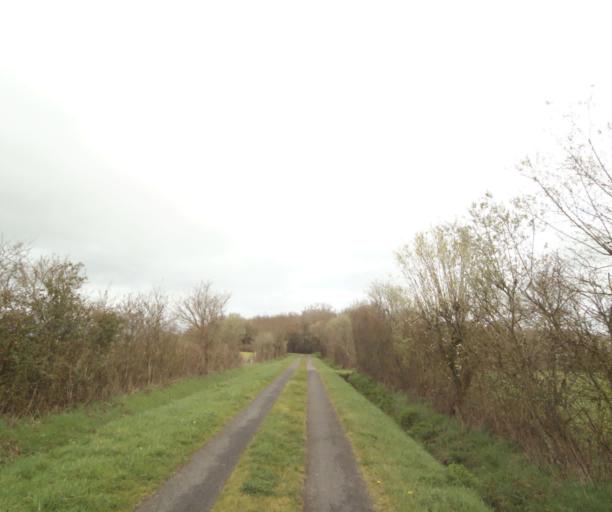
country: FR
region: Pays de la Loire
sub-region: Departement de la Loire-Atlantique
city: Bouvron
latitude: 47.4271
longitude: -1.8921
